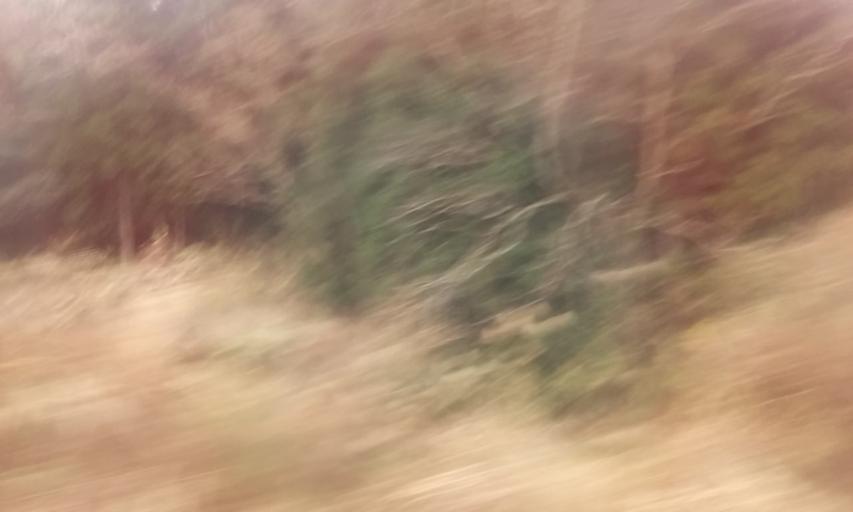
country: JP
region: Gifu
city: Mizunami
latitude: 35.4151
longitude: 137.3144
